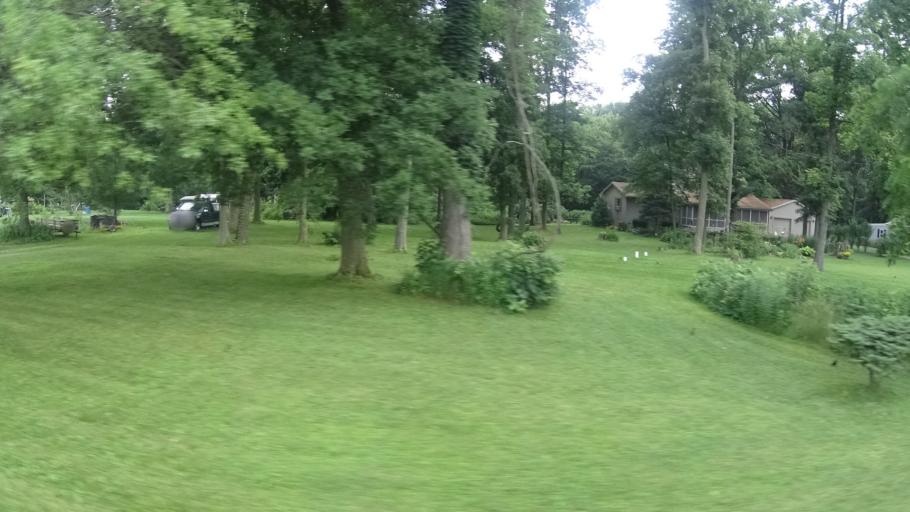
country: US
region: Ohio
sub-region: Erie County
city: Milan
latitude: 41.2968
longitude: -82.5056
